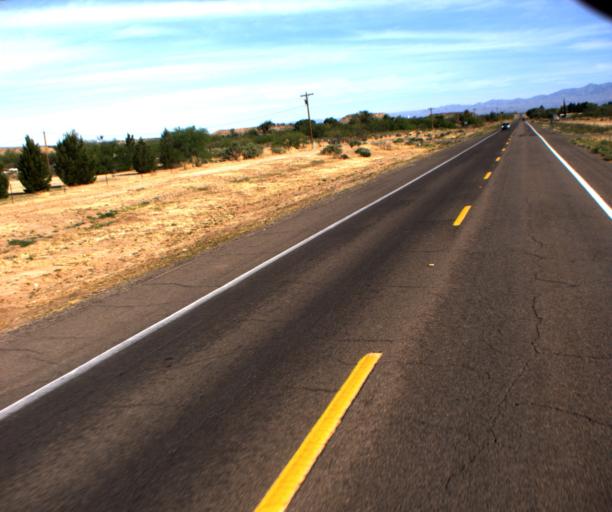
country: US
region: Arizona
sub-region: Graham County
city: Swift Trail Junction
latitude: 32.6905
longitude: -109.7077
